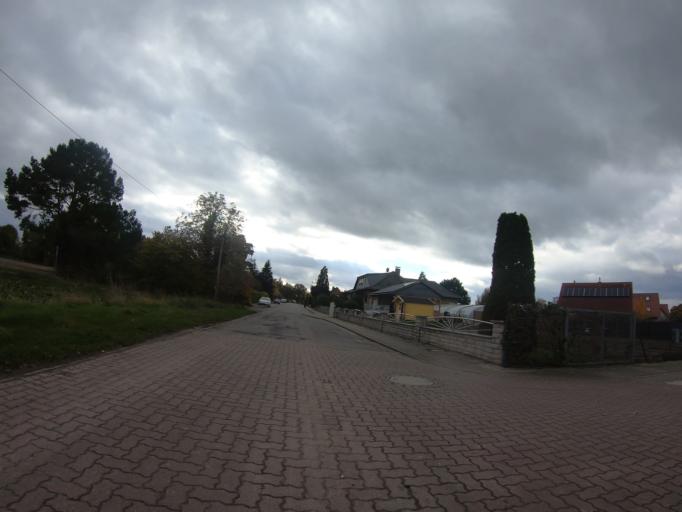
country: DE
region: Lower Saxony
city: Adenbuettel
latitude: 52.3801
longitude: 10.4835
